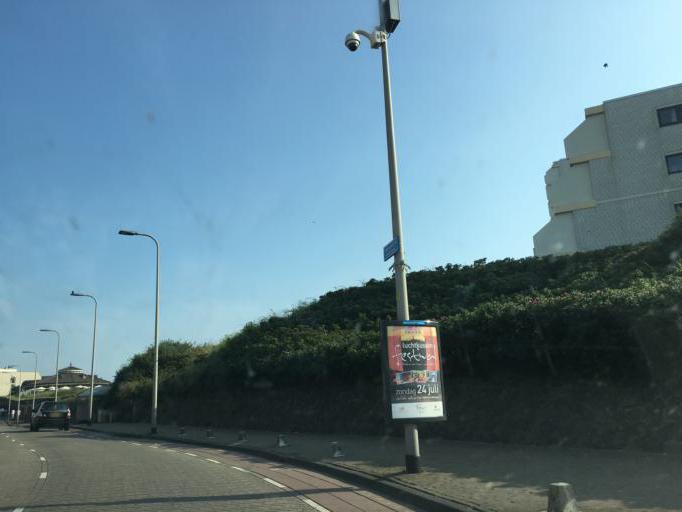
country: NL
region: South Holland
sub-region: Gemeente Noordwijk
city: Noordwijk-Binnen
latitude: 52.2431
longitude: 4.4293
